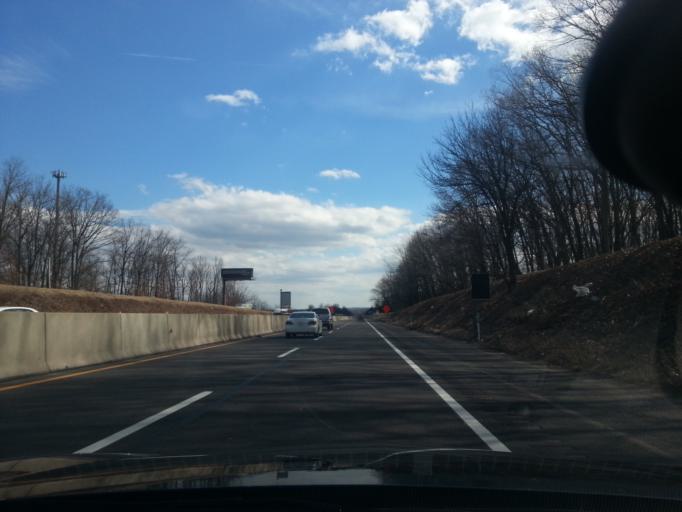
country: US
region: Pennsylvania
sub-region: Montgomery County
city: Harleysville
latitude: 40.2817
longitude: -75.3618
